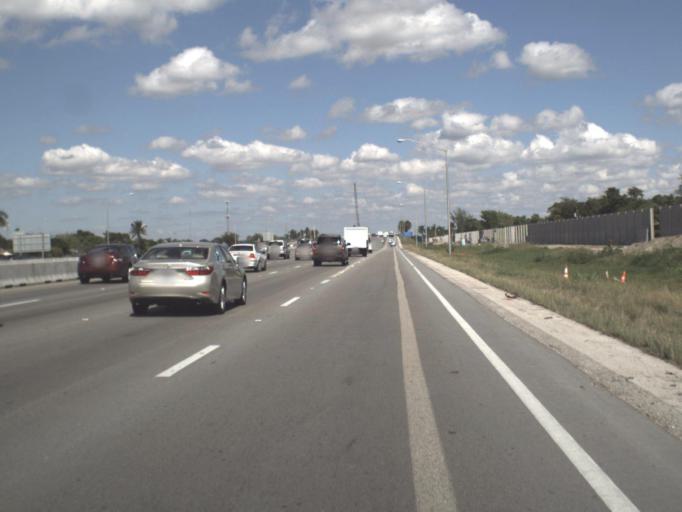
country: US
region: Florida
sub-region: Miami-Dade County
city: South Miami Heights
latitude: 25.6064
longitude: -80.3779
